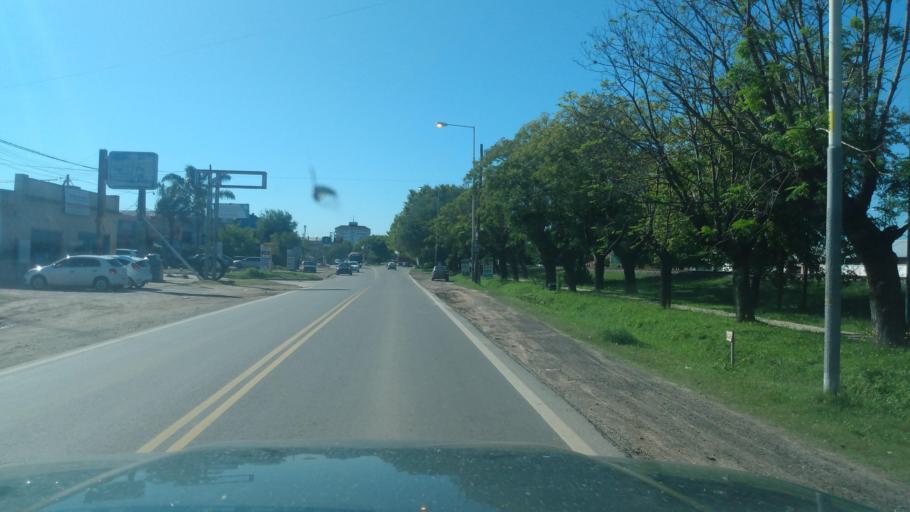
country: AR
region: Buenos Aires
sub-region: Partido de General Rodriguez
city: General Rodriguez
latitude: -34.6069
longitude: -58.9607
